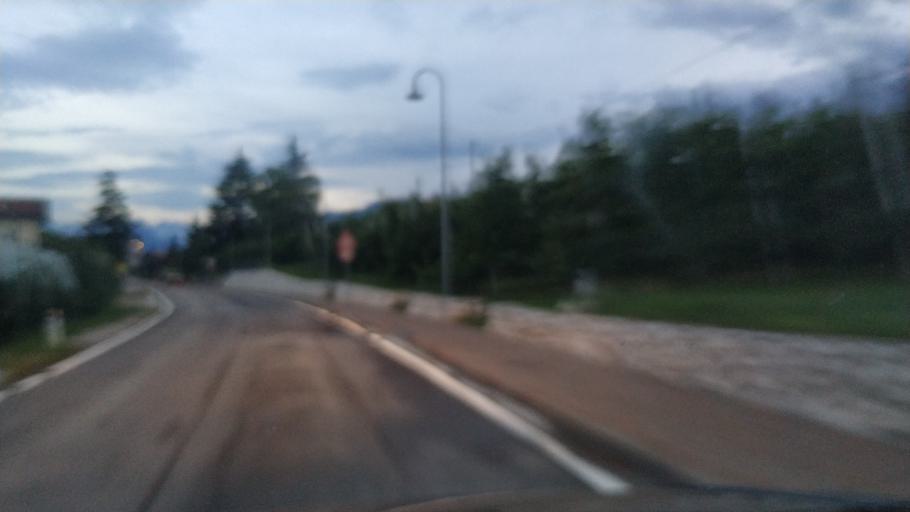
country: IT
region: Trentino-Alto Adige
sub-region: Provincia di Trento
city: Romallo
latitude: 46.4012
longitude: 11.0697
